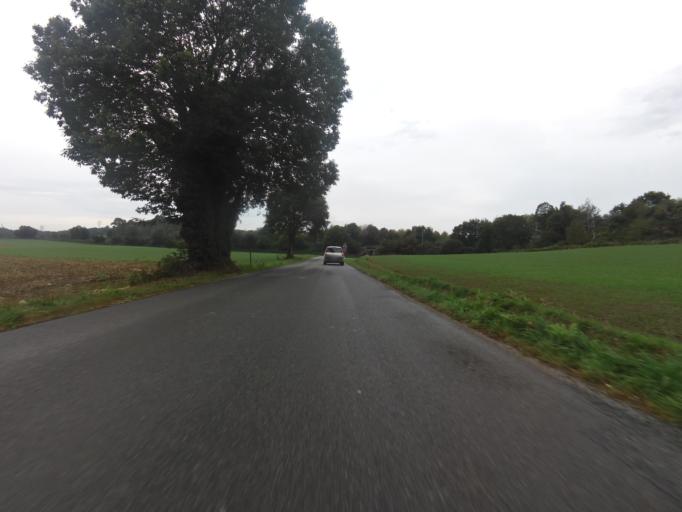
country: FR
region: Brittany
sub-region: Departement du Morbihan
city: Saint-Ave
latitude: 47.6858
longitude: -2.7147
